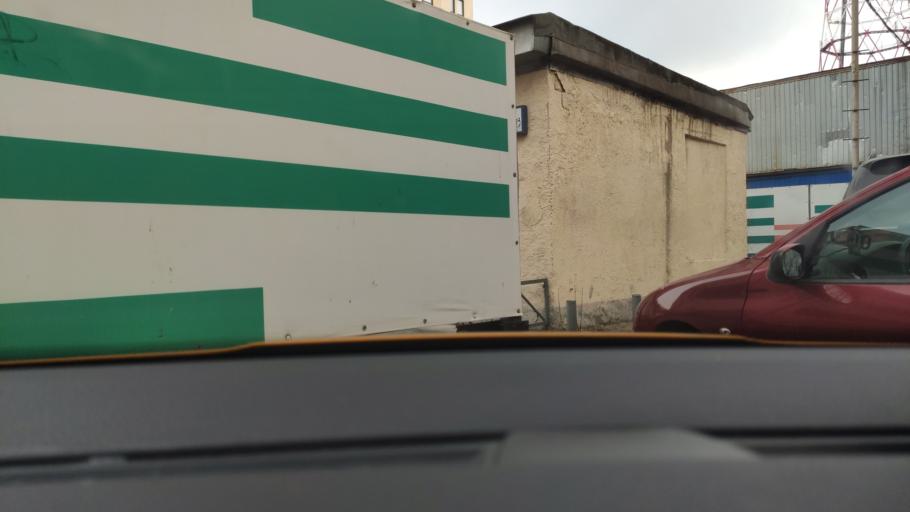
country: RU
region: Moskovskaya
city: Khoroshevo-Mnevniki
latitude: 55.7794
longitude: 37.4904
